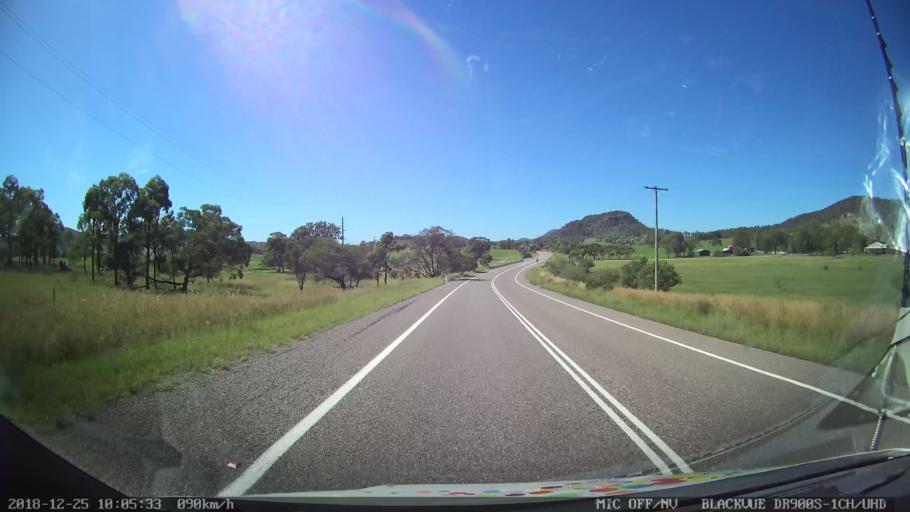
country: AU
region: New South Wales
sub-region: Upper Hunter Shire
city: Merriwa
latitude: -32.2486
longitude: 150.4866
